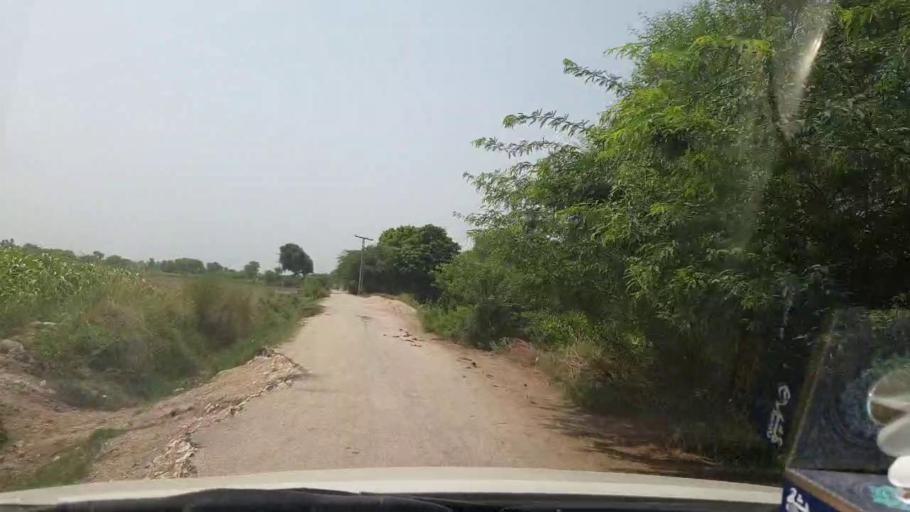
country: PK
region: Sindh
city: Shikarpur
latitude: 27.9926
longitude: 68.7125
